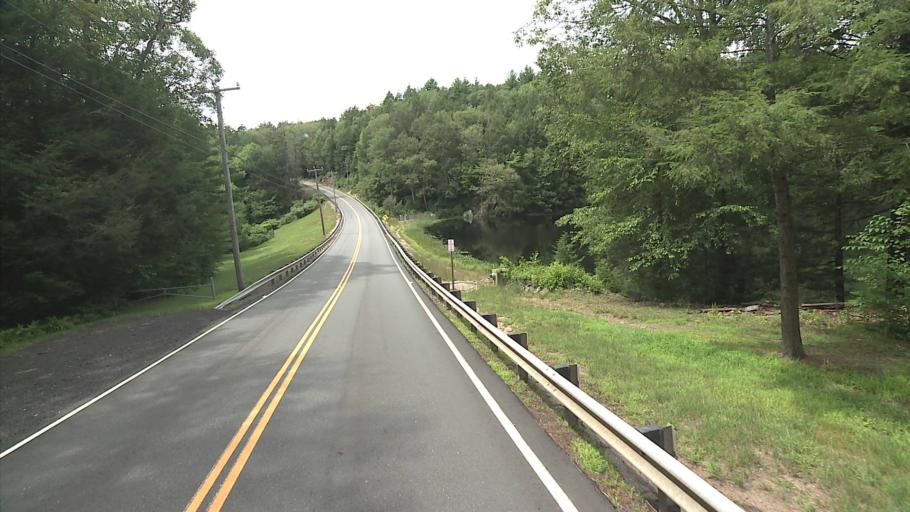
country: US
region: Massachusetts
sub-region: Hampden County
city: Holland
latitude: 41.9915
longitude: -72.1311
